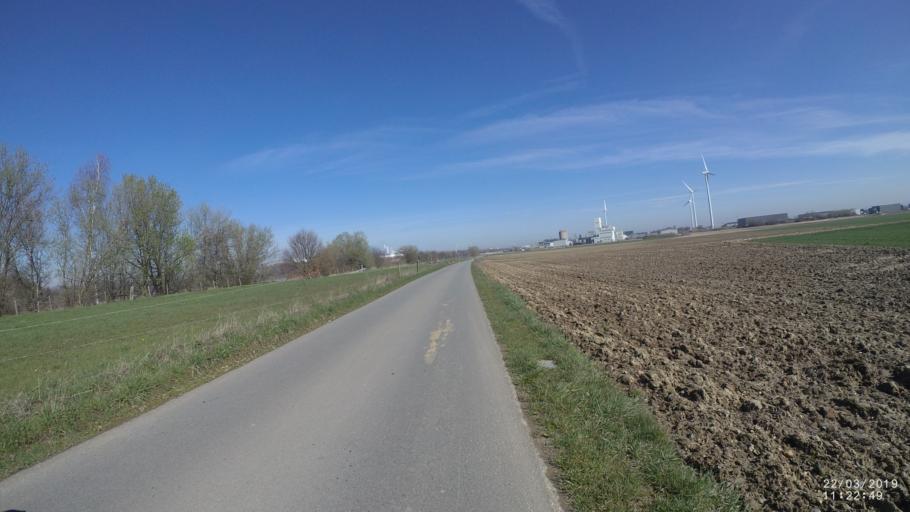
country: BE
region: Flanders
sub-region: Provincie Limburg
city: Lanaken
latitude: 50.8734
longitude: 5.6434
